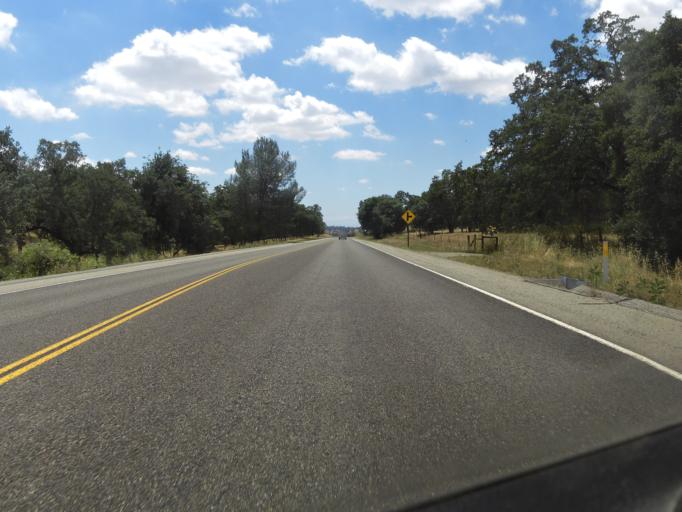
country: US
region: California
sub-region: Madera County
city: Yosemite Lakes
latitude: 37.1366
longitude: -119.6846
